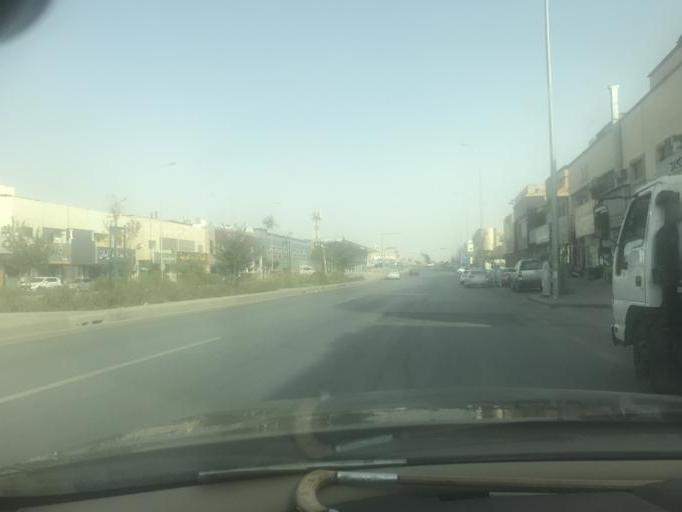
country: SA
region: Ar Riyad
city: Riyadh
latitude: 24.7419
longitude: 46.7782
